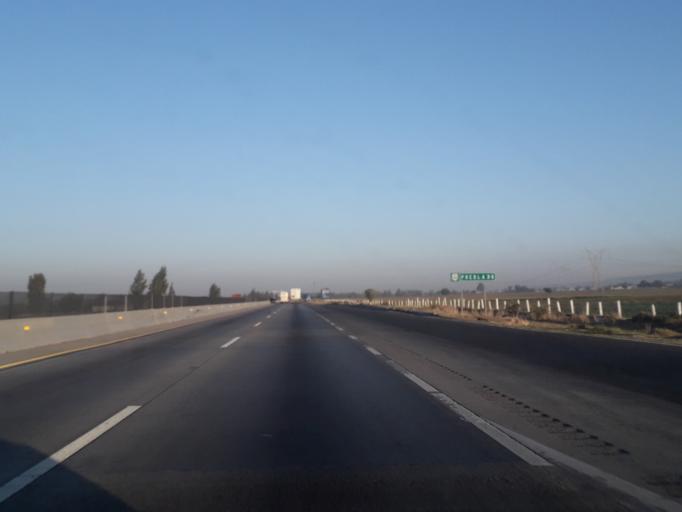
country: MX
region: Puebla
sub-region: Tepeaca
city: San Jose Carpinteros
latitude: 19.0088
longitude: -97.9079
